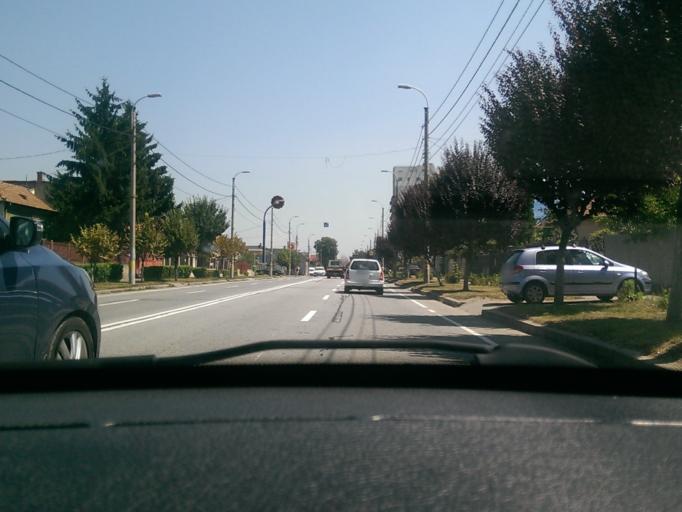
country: RO
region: Cluj
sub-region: Municipiul Cluj-Napoca
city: Cluj-Napoca
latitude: 46.7872
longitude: 23.5766
